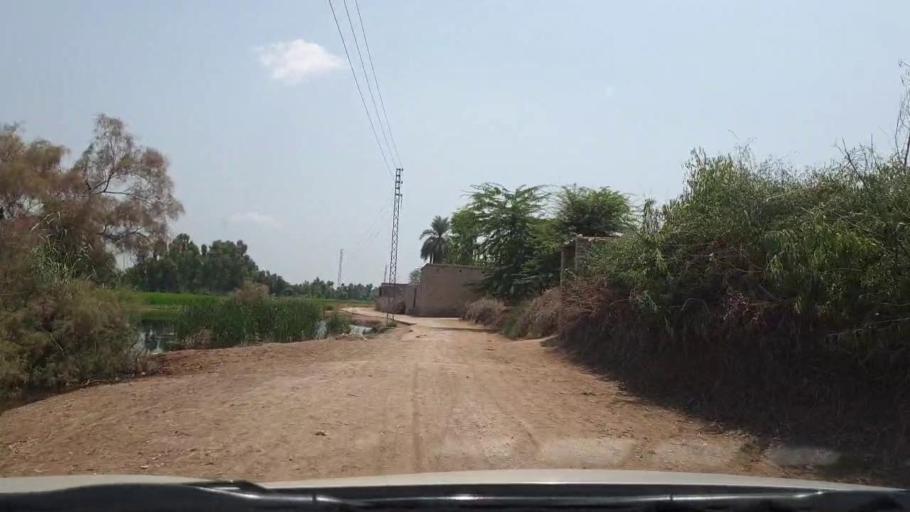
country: PK
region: Sindh
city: New Badah
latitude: 27.2974
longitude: 68.0696
